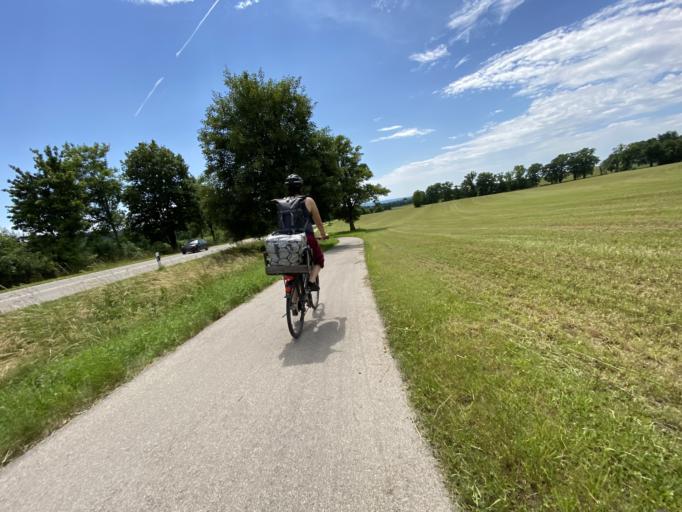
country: DE
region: Bavaria
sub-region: Upper Bavaria
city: Wessling
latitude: 48.0625
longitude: 11.2392
